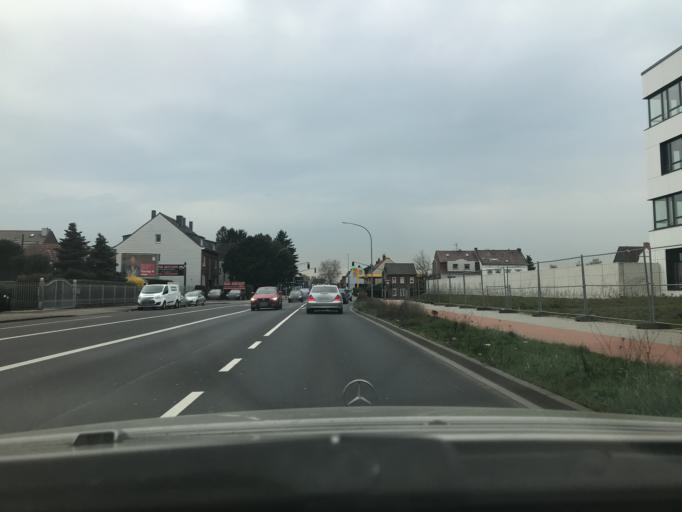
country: DE
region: North Rhine-Westphalia
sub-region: Regierungsbezirk Dusseldorf
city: Korschenbroich
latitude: 51.2215
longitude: 6.4803
